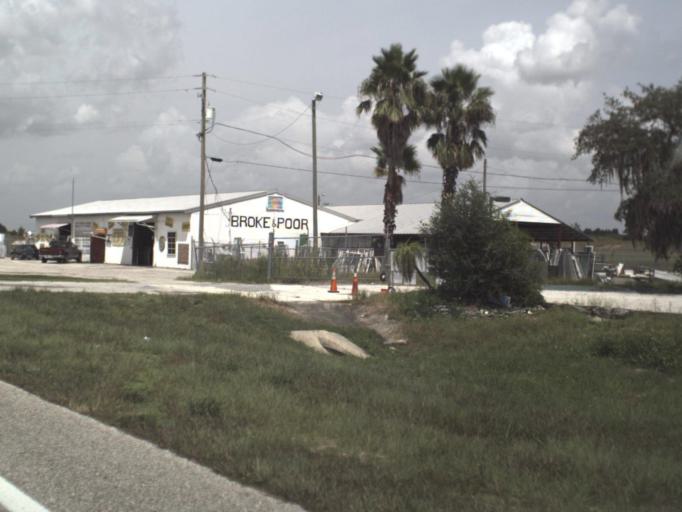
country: US
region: Florida
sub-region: Polk County
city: Crooked Lake Park
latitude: 27.8569
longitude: -81.5870
